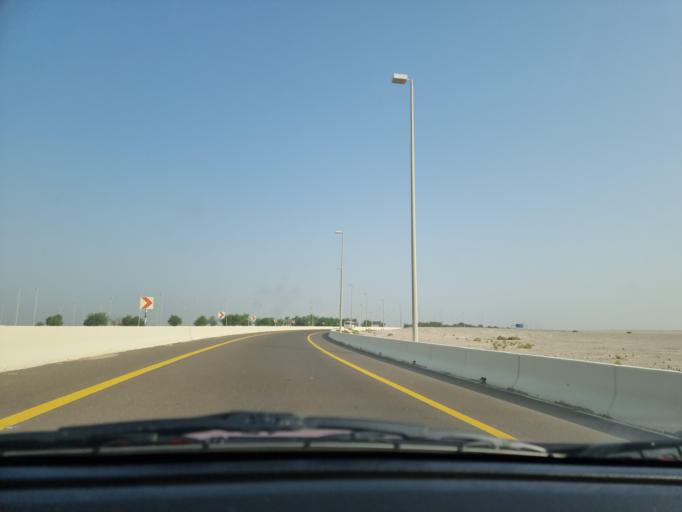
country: AE
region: Abu Dhabi
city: Abu Dhabi
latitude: 24.4118
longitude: 54.6775
